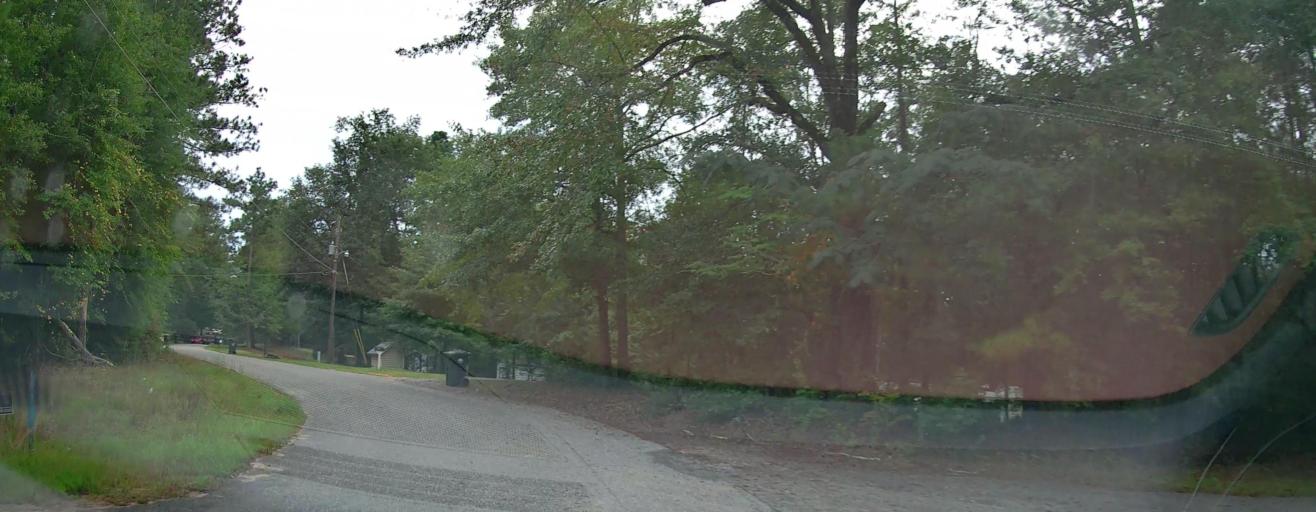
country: US
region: Georgia
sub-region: Peach County
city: Byron
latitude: 32.6758
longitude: -83.7156
